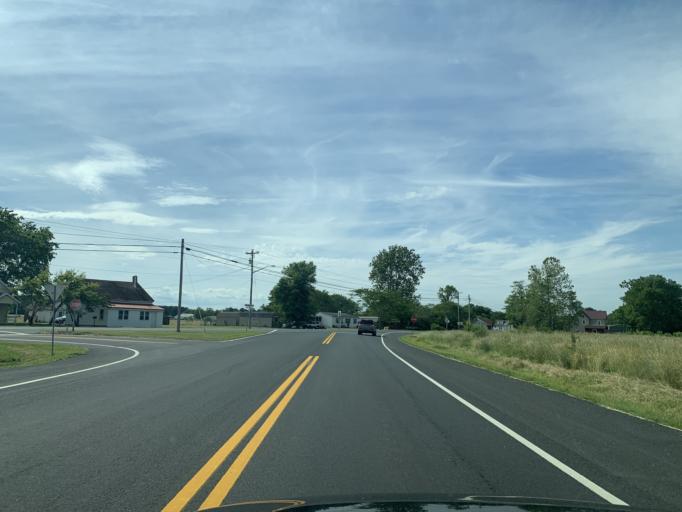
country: US
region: Maryland
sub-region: Wicomico County
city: Pittsville
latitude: 38.3235
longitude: -75.3729
